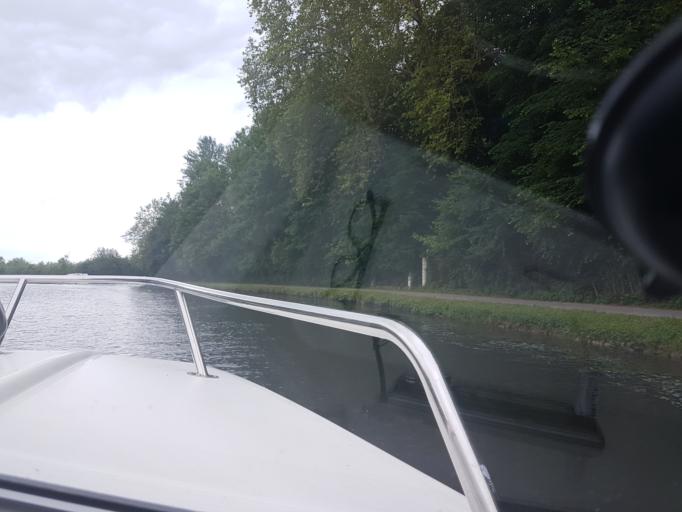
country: FR
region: Bourgogne
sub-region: Departement de l'Yonne
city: Champs-sur-Yonne
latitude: 47.7273
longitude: 3.6076
